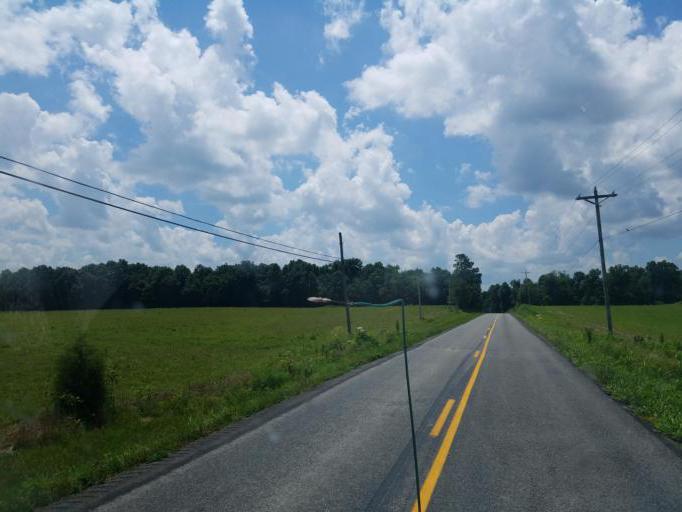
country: US
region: Kentucky
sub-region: Grayson County
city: Leitchfield
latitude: 37.5123
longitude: -86.4723
